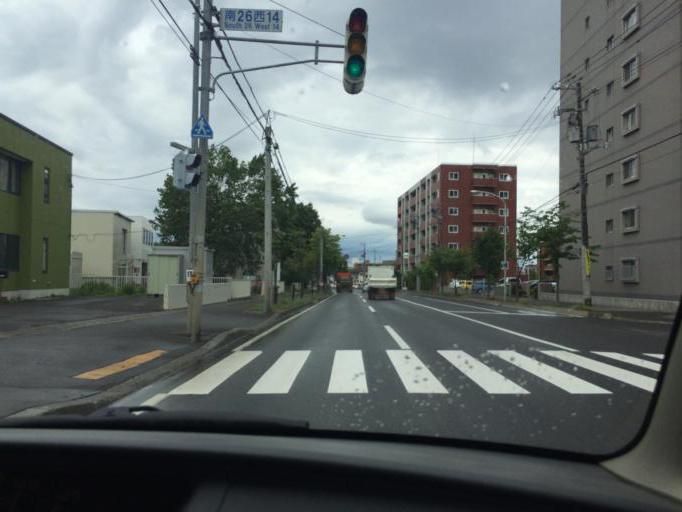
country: JP
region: Hokkaido
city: Sapporo
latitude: 43.0237
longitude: 141.3421
